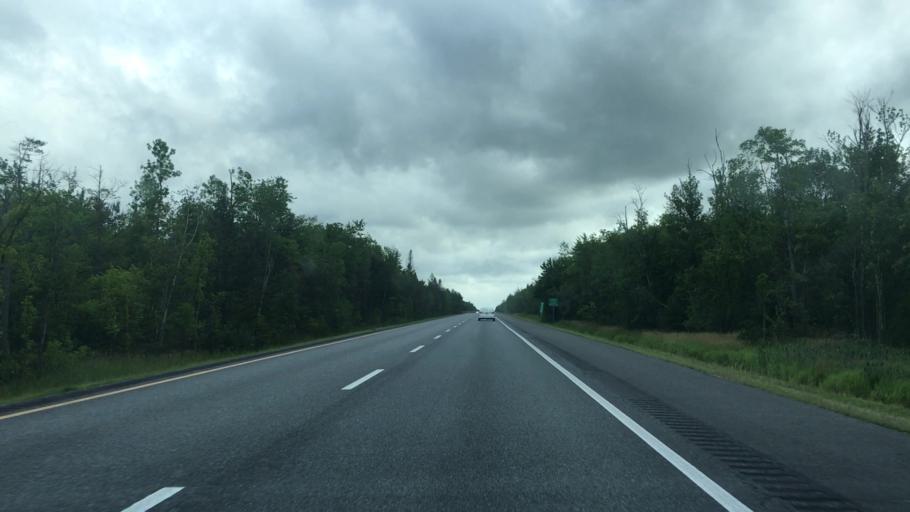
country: US
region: Maine
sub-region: Waldo County
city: Burnham
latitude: 44.6854
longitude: -69.4757
